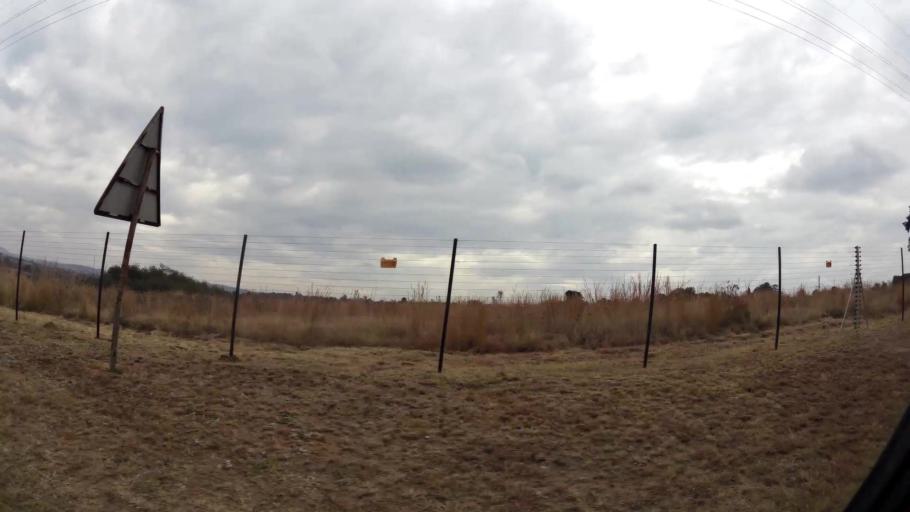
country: ZA
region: Gauteng
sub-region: West Rand District Municipality
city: Muldersdriseloop
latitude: -26.0571
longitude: 27.8818
